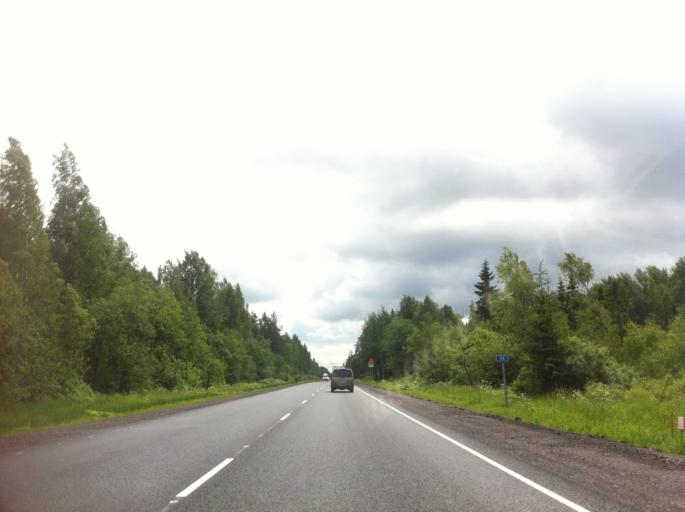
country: RU
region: Leningrad
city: Rozhdestveno
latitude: 59.2273
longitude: 29.9273
